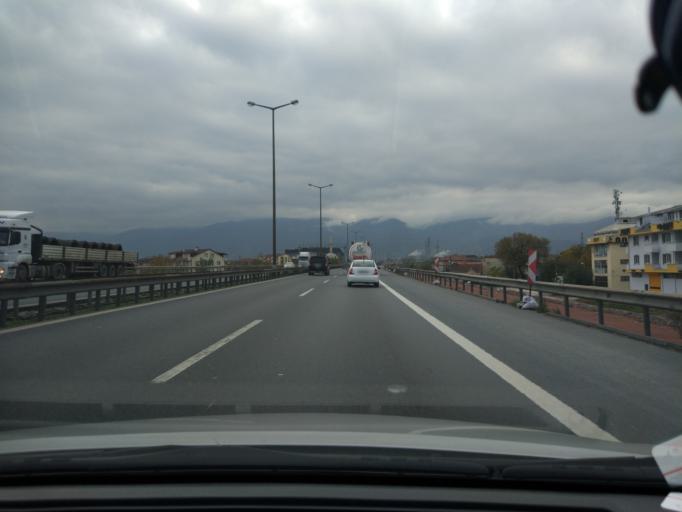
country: TR
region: Kocaeli
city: Kosekoy
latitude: 40.7560
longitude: 30.0376
